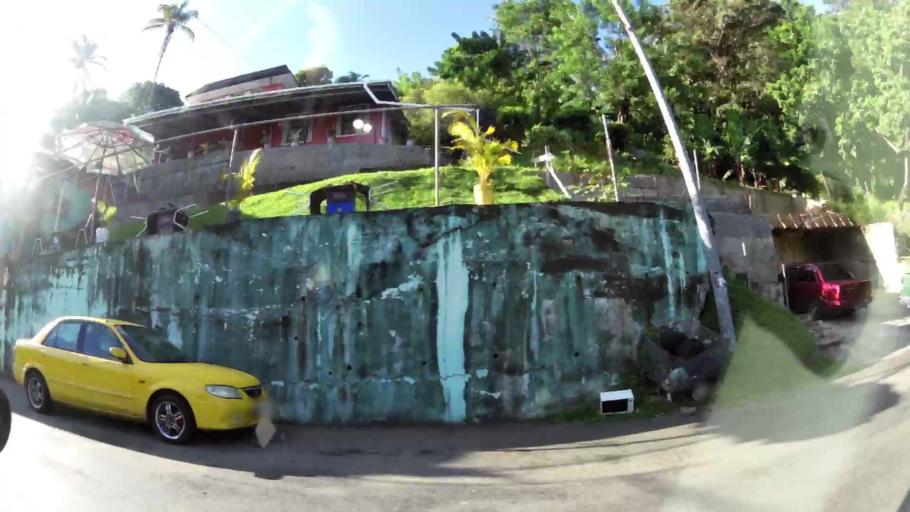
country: TT
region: Eastern Tobago
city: Roxborough
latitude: 11.2321
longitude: -60.6052
